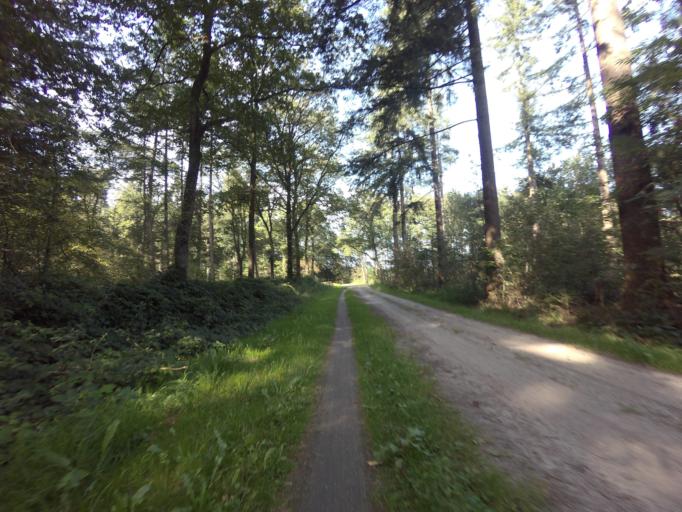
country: NL
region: Drenthe
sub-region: Gemeente Tynaarlo
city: Vries
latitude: 53.0677
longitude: 6.5069
